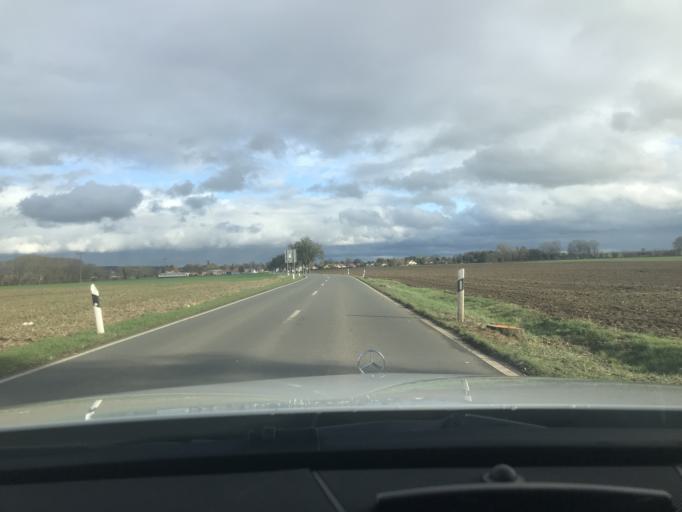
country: DE
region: Thuringia
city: Bufleben
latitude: 50.9990
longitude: 10.7225
